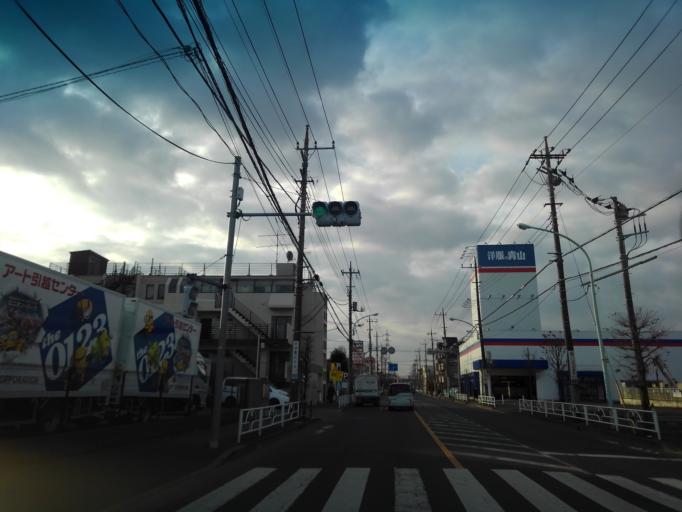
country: JP
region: Tokyo
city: Tanashicho
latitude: 35.7251
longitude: 139.5107
